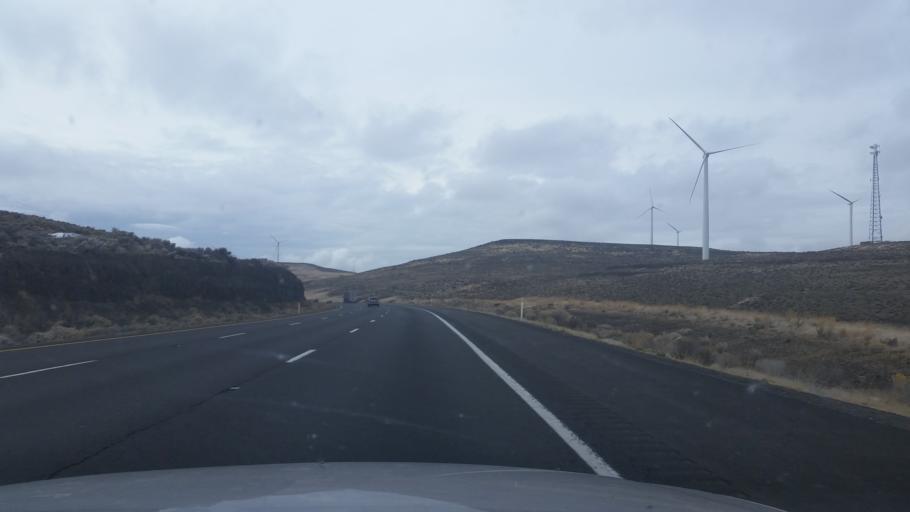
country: US
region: Washington
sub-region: Kittitas County
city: Kittitas
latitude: 46.9432
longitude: -120.1460
